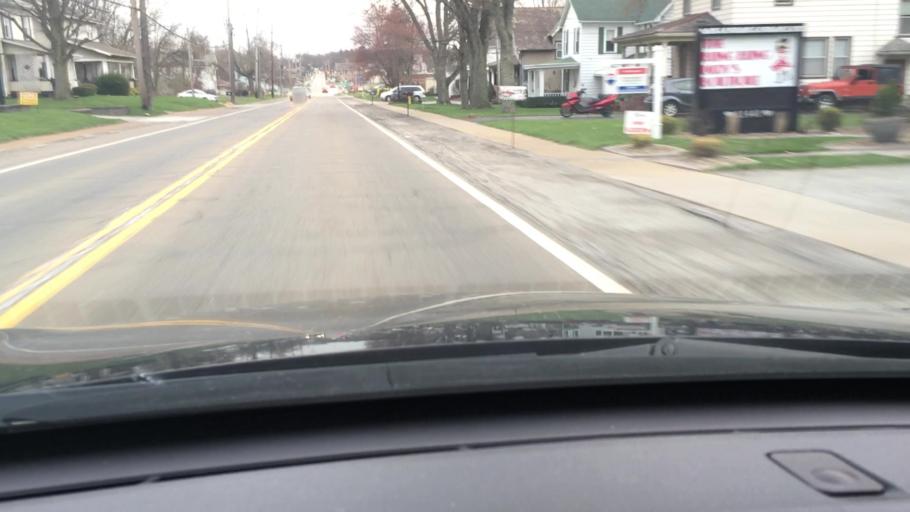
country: US
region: Ohio
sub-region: Mahoning County
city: Boardman
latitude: 40.9521
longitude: -80.6592
